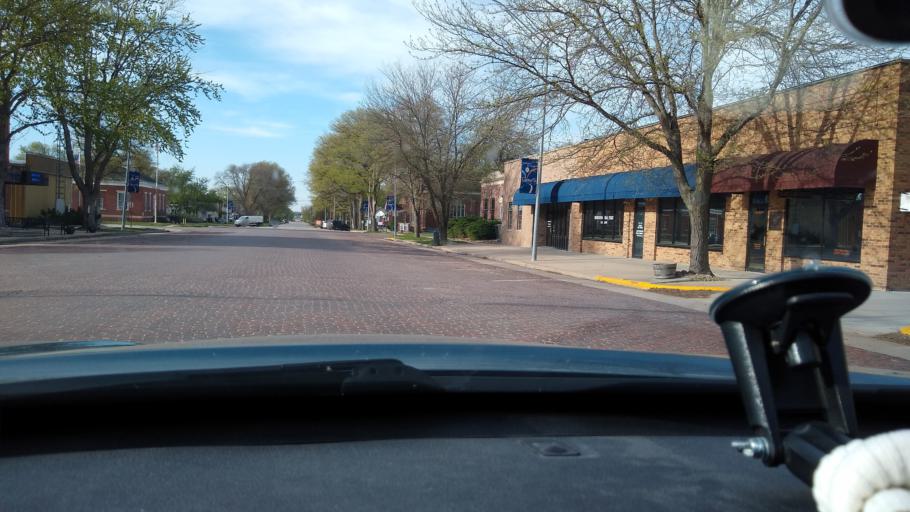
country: US
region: Nebraska
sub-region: Fillmore County
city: Geneva
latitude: 40.5263
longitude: -97.6028
